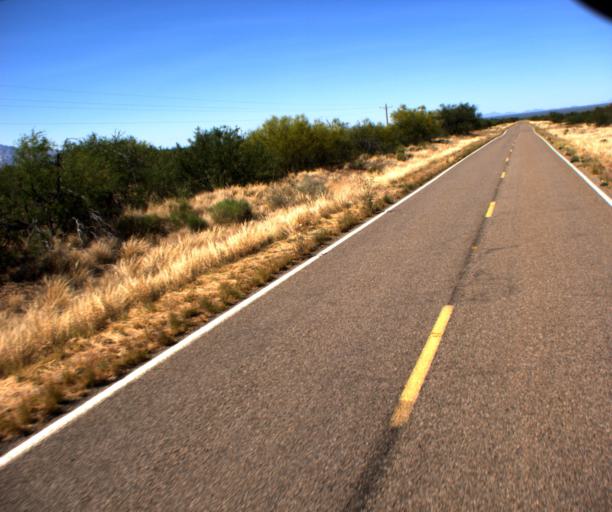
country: US
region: Arizona
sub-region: Pima County
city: Three Points
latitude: 31.7836
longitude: -111.4588
